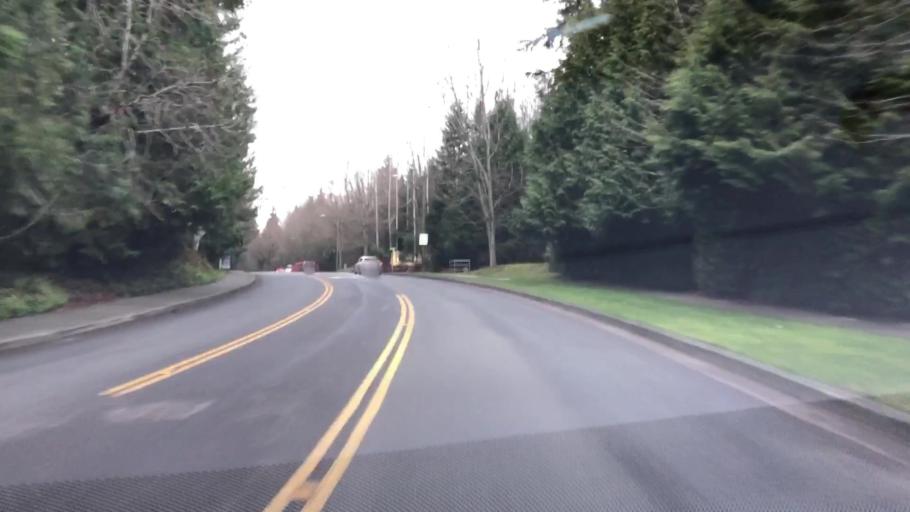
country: US
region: Washington
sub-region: Snohomish County
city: Mill Creek
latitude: 47.8573
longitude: -122.2145
